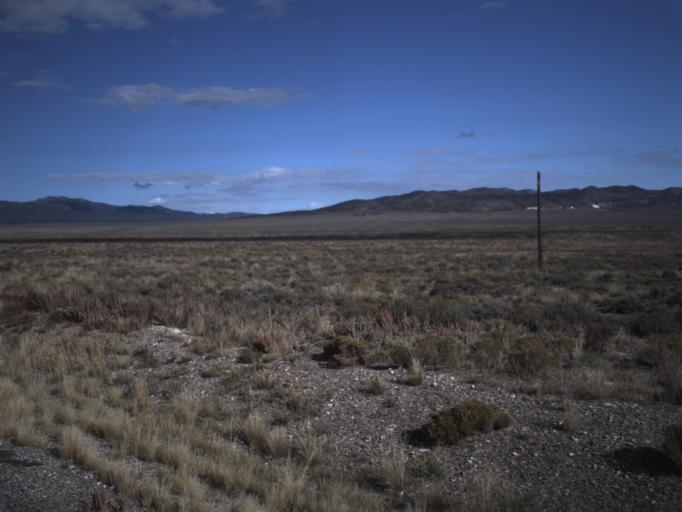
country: US
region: Utah
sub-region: Beaver County
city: Milford
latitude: 38.4297
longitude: -113.1252
